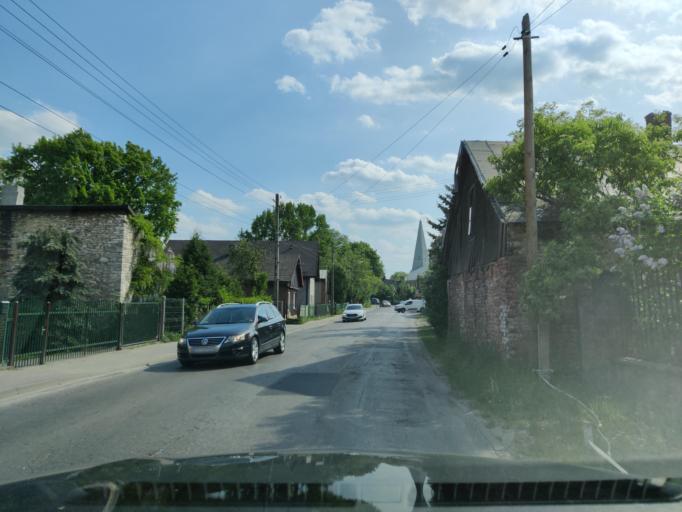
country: PL
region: Silesian Voivodeship
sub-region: Dabrowa Gornicza
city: Dabrowa Gornicza
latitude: 50.3923
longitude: 19.2417
